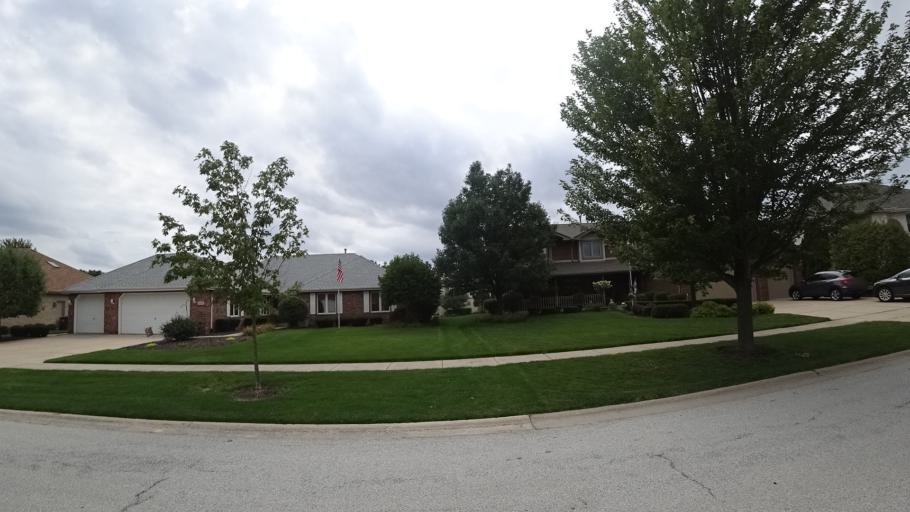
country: US
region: Illinois
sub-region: Cook County
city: Tinley Park
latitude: 41.5685
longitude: -87.8095
